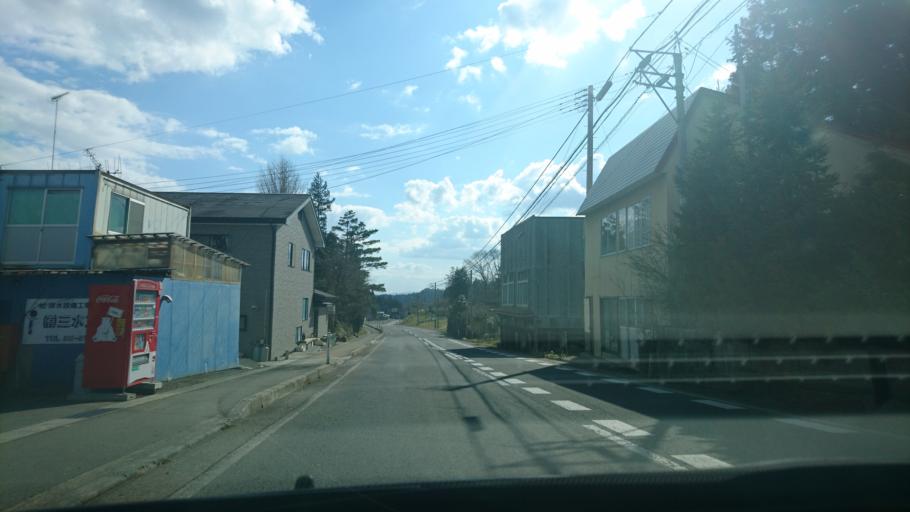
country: JP
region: Iwate
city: Kitakami
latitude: 39.2545
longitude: 141.2098
